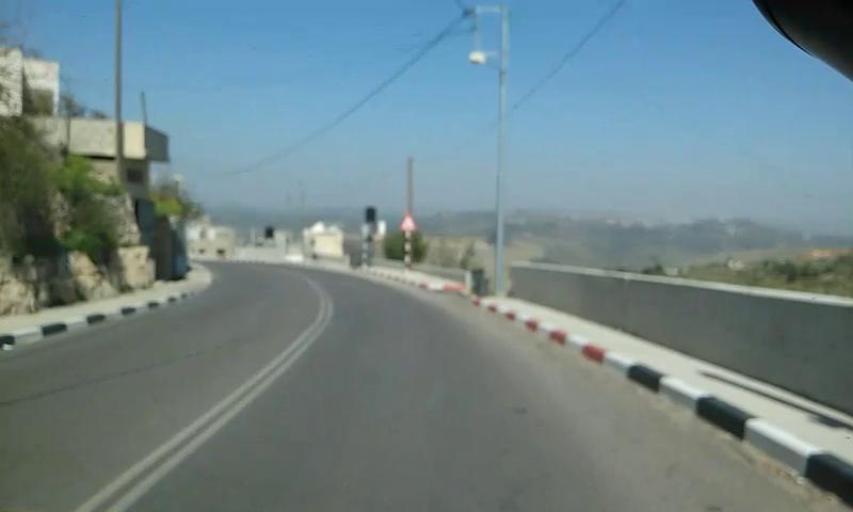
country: PS
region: West Bank
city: Husan
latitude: 31.7080
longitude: 35.1480
